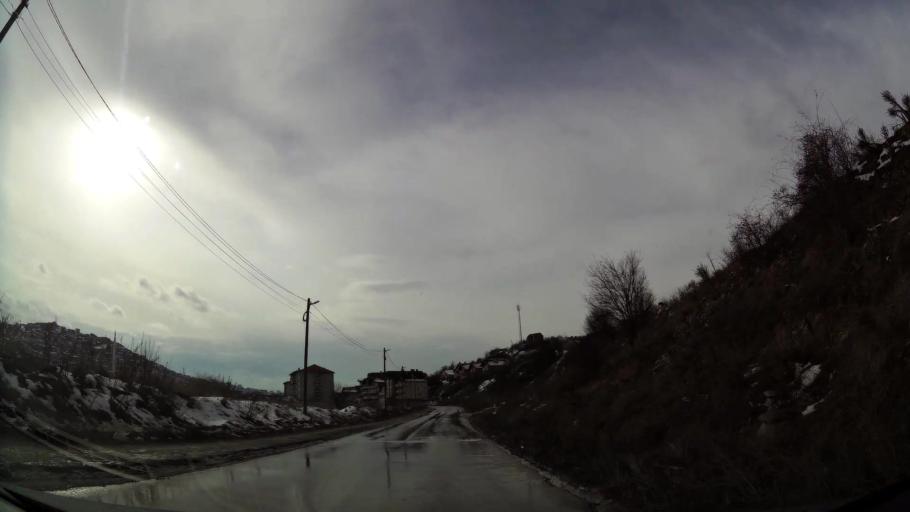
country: XK
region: Pristina
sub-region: Komuna e Prishtines
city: Pristina
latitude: 42.6852
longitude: 21.1755
